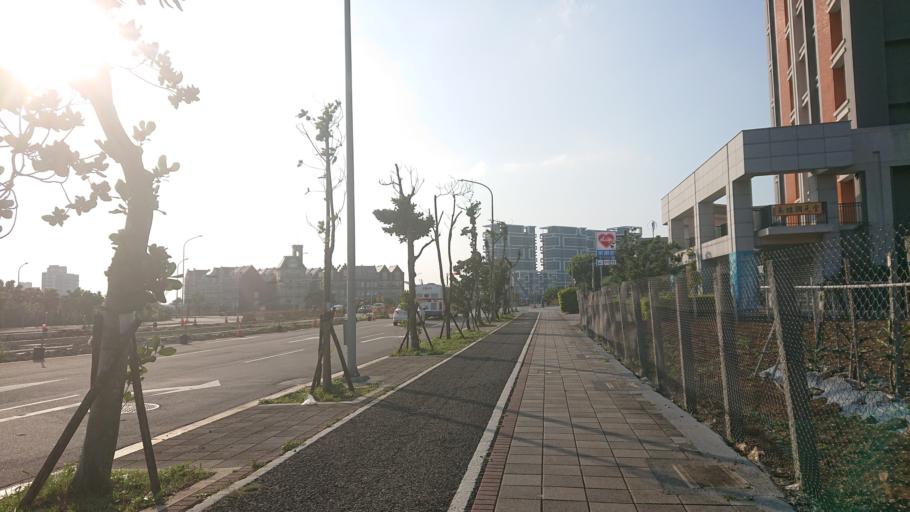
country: TW
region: Taipei
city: Taipei
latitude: 25.1911
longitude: 121.4282
